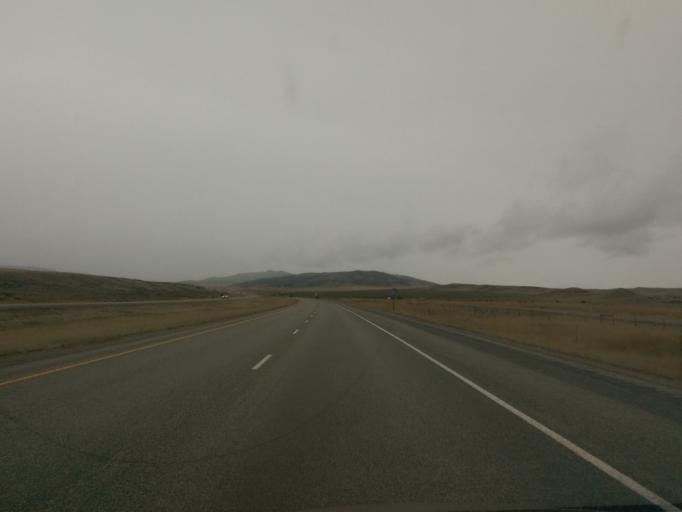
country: US
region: Montana
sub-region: Gallatin County
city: Three Forks
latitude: 45.9149
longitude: -111.7508
